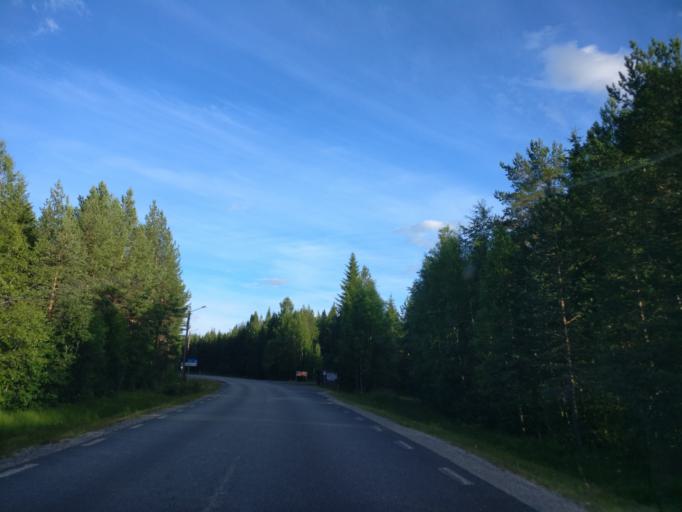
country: SE
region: Jaemtland
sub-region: Braecke Kommun
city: Braecke
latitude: 62.4212
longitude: 15.0000
